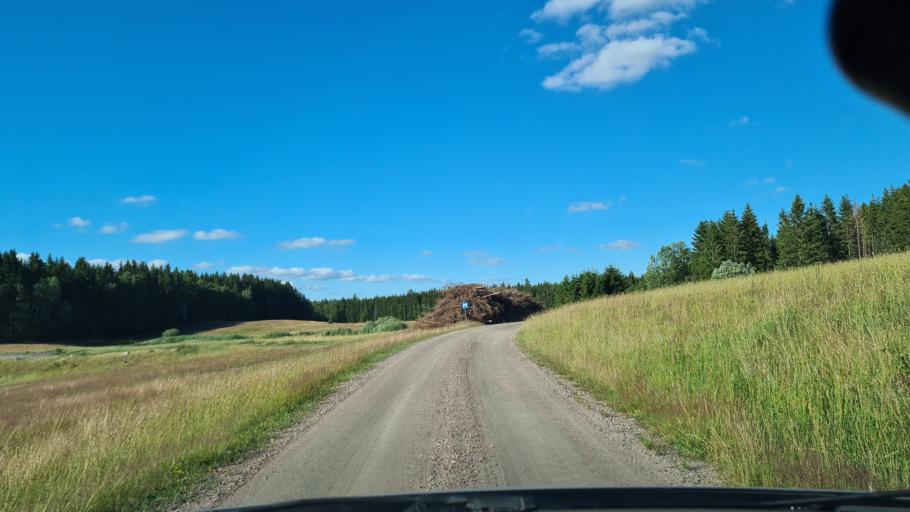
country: SE
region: Soedermanland
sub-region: Nykopings Kommun
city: Stigtomta
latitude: 58.9250
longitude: 16.8910
